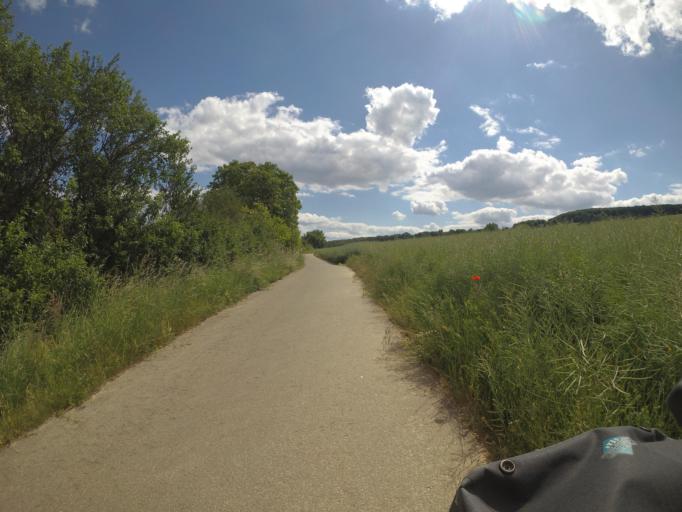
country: DE
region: Rheinland-Pfalz
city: Katzenbach
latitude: 49.6528
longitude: 7.8210
